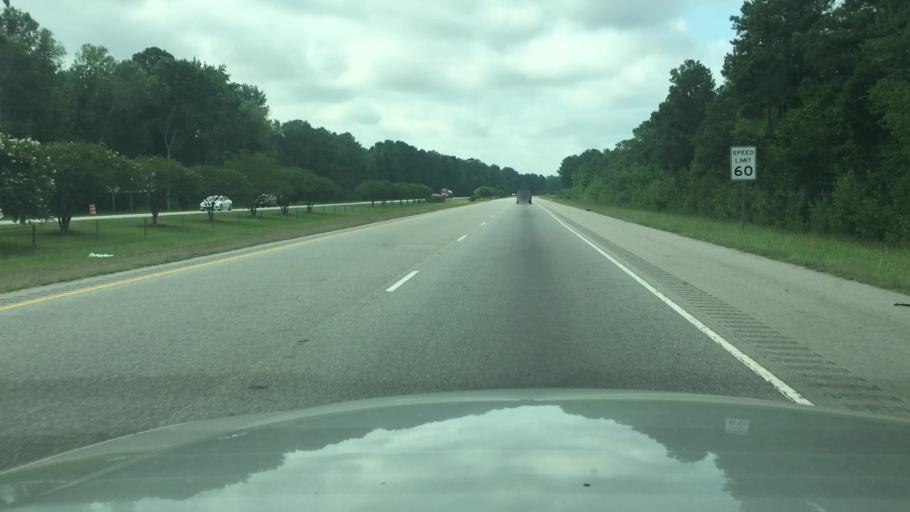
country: US
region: North Carolina
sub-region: Cumberland County
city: Fayetteville
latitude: 35.0008
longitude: -78.8652
